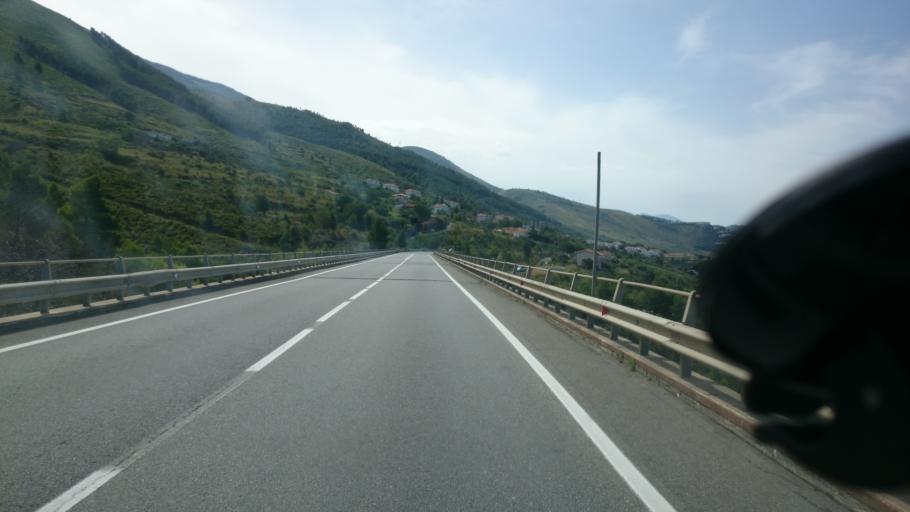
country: IT
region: Calabria
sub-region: Provincia di Cosenza
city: Praia a Mare
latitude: 39.8923
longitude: 15.7897
